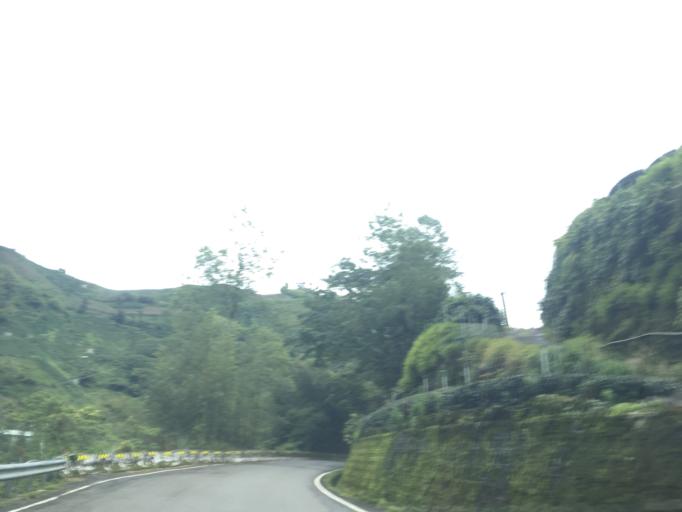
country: TW
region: Taiwan
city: Lugu
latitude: 23.5331
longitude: 120.7005
